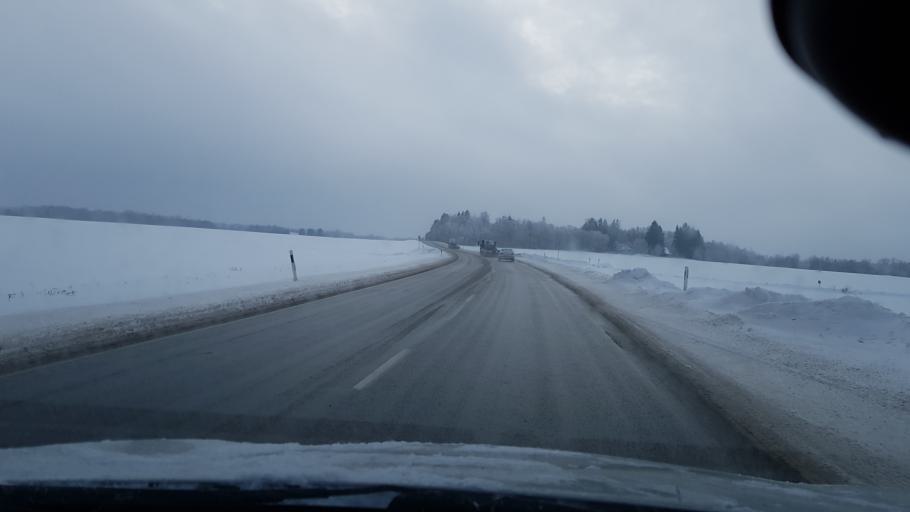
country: EE
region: Harju
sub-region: Saue linn
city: Saue
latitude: 59.3449
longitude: 24.4809
